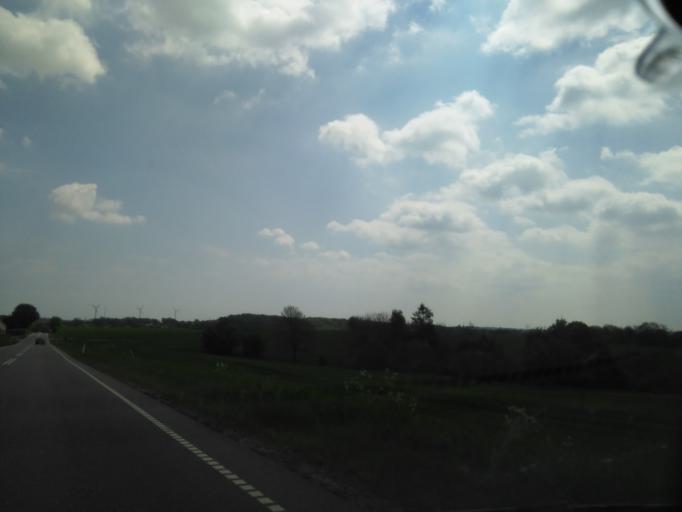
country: DK
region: Central Jutland
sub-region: Skanderborg Kommune
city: Stilling
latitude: 55.9968
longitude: 10.0133
